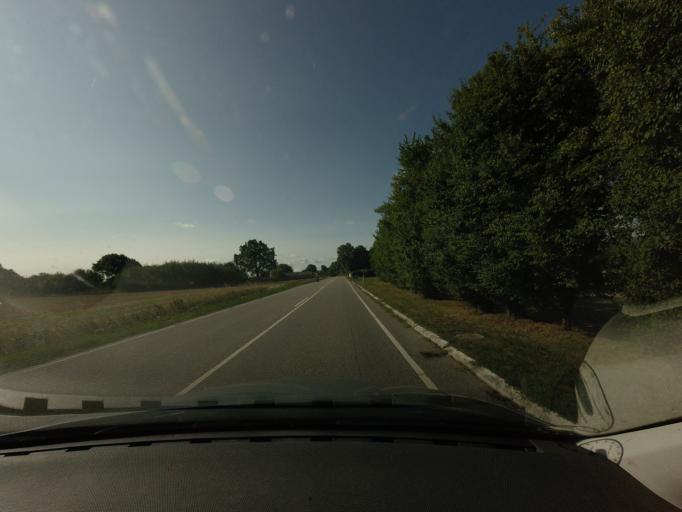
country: DK
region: Zealand
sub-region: Vordingborg Kommune
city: Praesto
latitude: 55.0839
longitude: 12.0823
